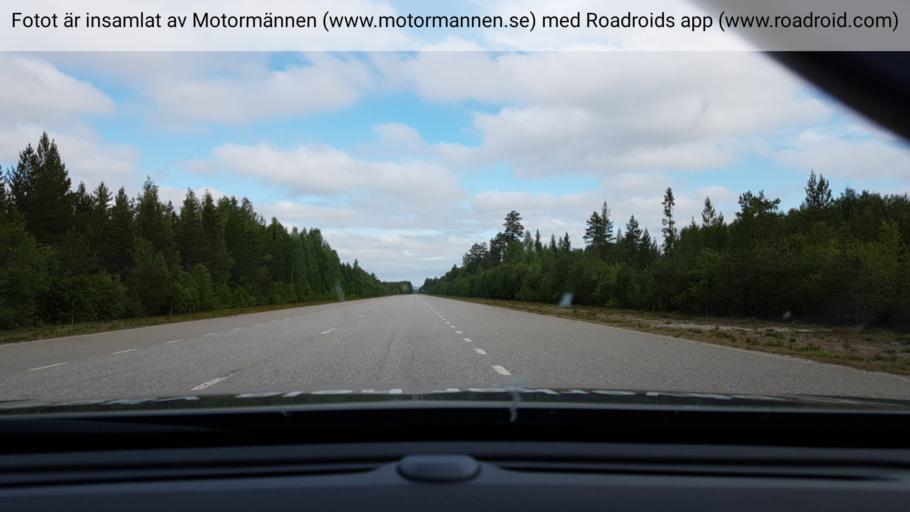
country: SE
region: Vaesterbotten
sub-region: Norsjo Kommun
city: Norsjoe
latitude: 64.5691
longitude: 19.3121
